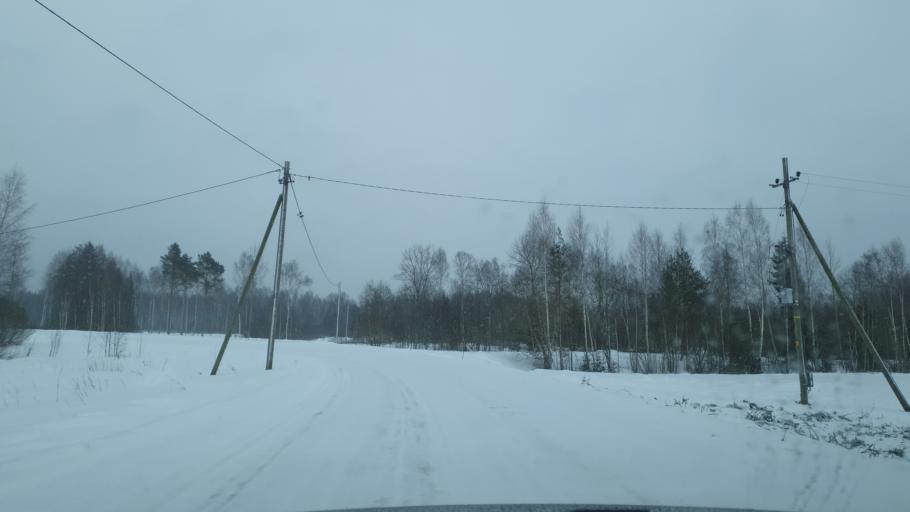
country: EE
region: Jogevamaa
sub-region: Tabivere vald
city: Tabivere
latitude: 58.5748
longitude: 26.7944
